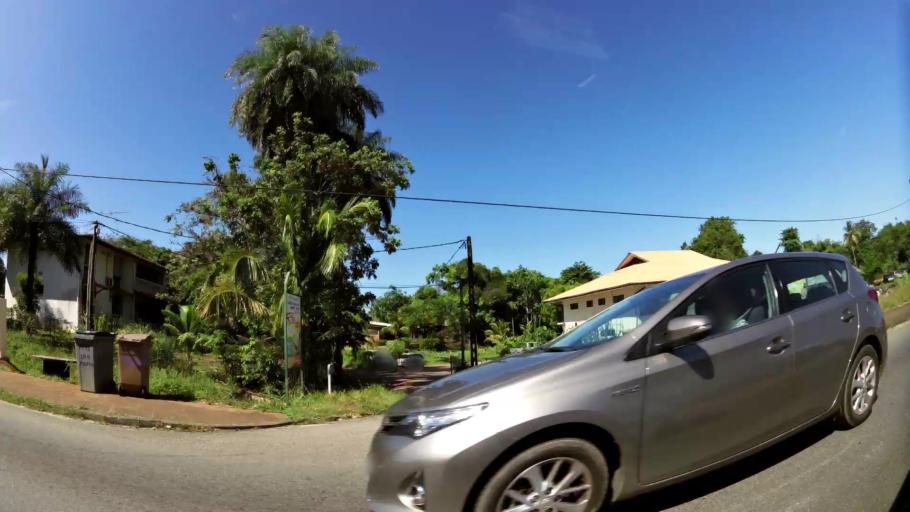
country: GF
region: Guyane
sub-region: Guyane
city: Remire-Montjoly
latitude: 4.9201
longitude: -52.2793
